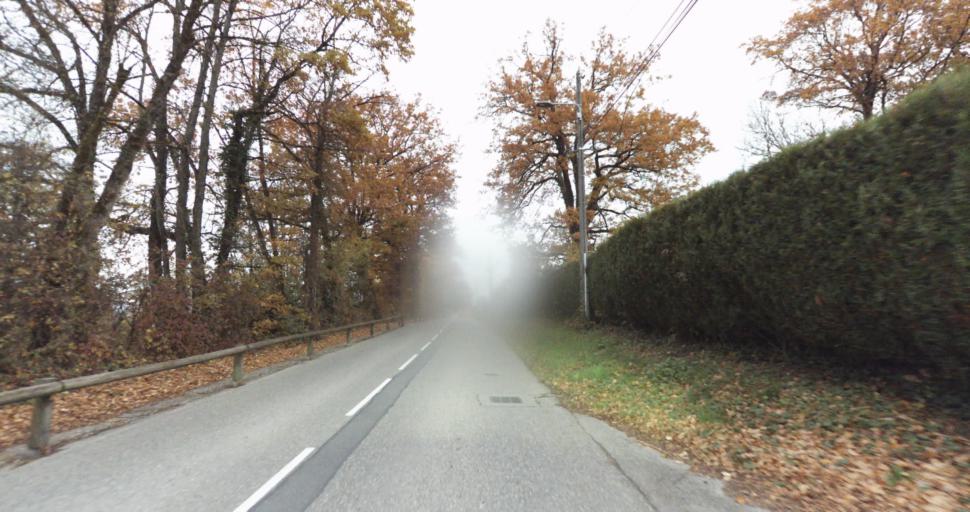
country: FR
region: Rhone-Alpes
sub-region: Departement de la Haute-Savoie
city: Saint-Felix
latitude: 45.8071
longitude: 5.9726
